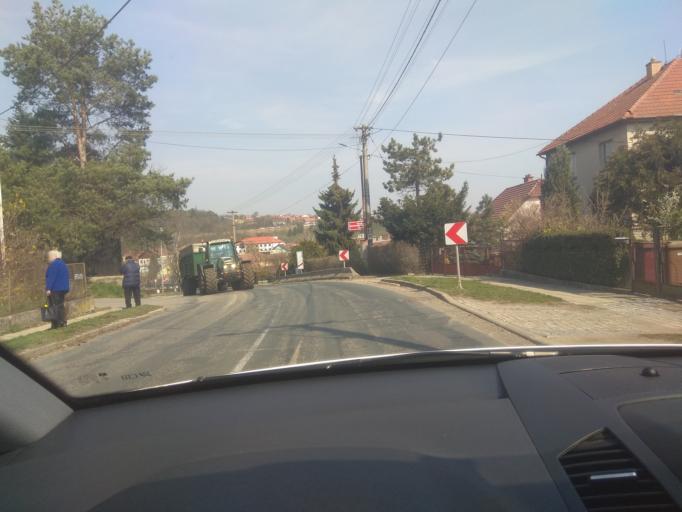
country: CZ
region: South Moravian
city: Zastavka
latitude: 49.1849
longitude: 16.3619
